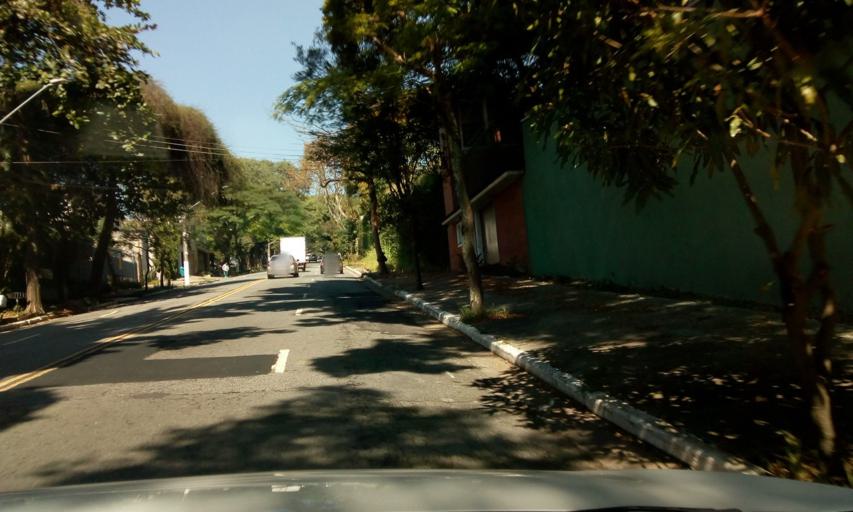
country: BR
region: Sao Paulo
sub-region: Sao Paulo
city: Sao Paulo
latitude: -23.5812
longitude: -46.7058
